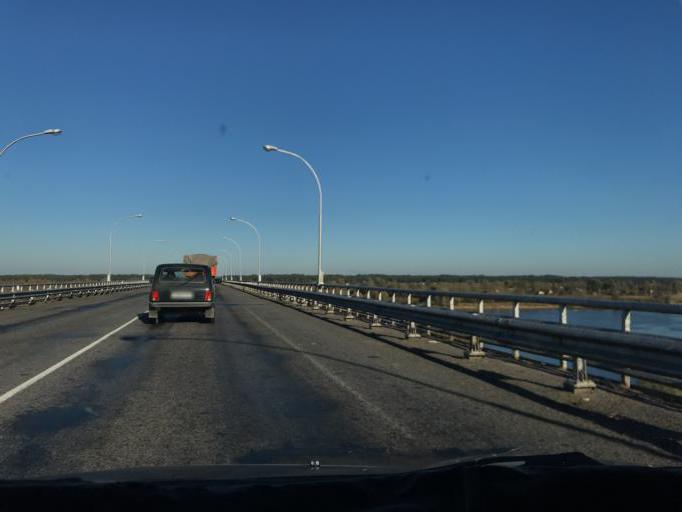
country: BY
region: Gomel
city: Mazyr
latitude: 52.0235
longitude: 29.3179
